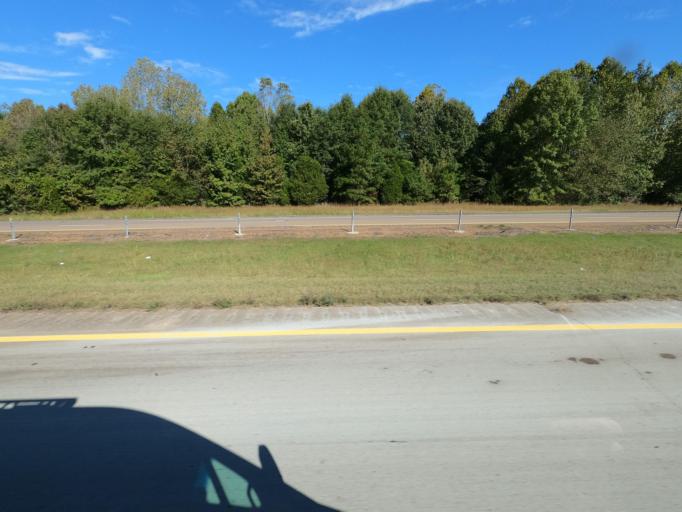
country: US
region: Tennessee
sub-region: Shelby County
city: Lakeland
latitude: 35.3103
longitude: -89.7526
